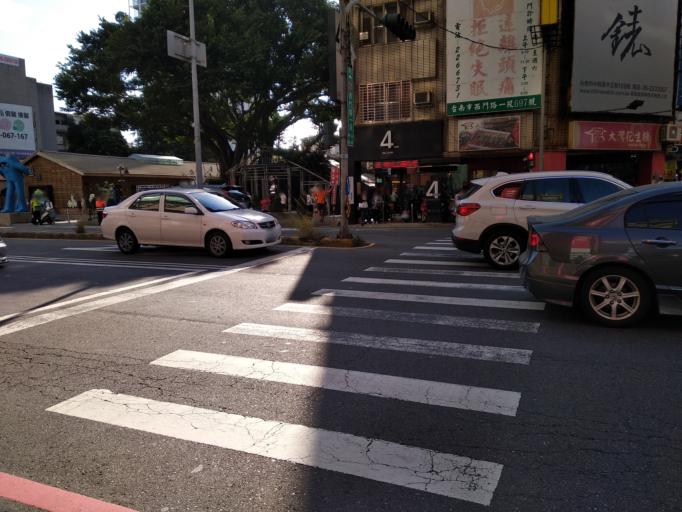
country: TW
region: Taiwan
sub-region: Tainan
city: Tainan
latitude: 22.9873
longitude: 120.1975
